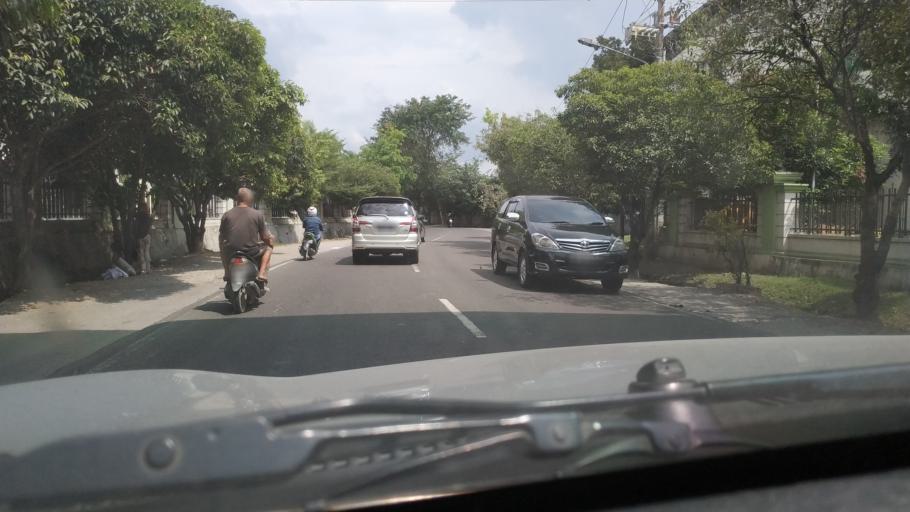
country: ID
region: North Sumatra
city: Sunggal
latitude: 3.5851
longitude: 98.6251
